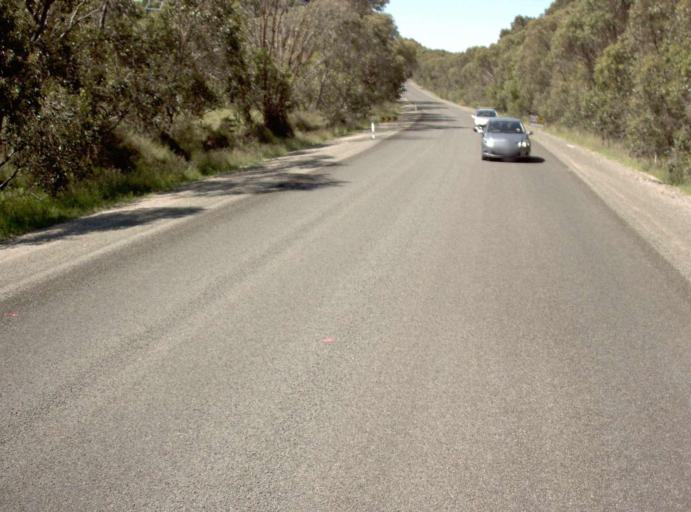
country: AU
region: Victoria
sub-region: Latrobe
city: Morwell
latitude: -38.7364
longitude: 146.1469
